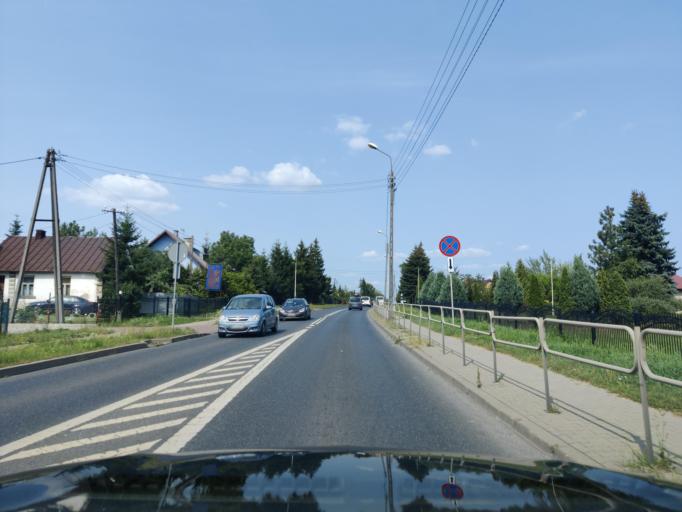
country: PL
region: Masovian Voivodeship
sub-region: Powiat pultuski
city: Pultusk
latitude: 52.7185
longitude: 21.0850
